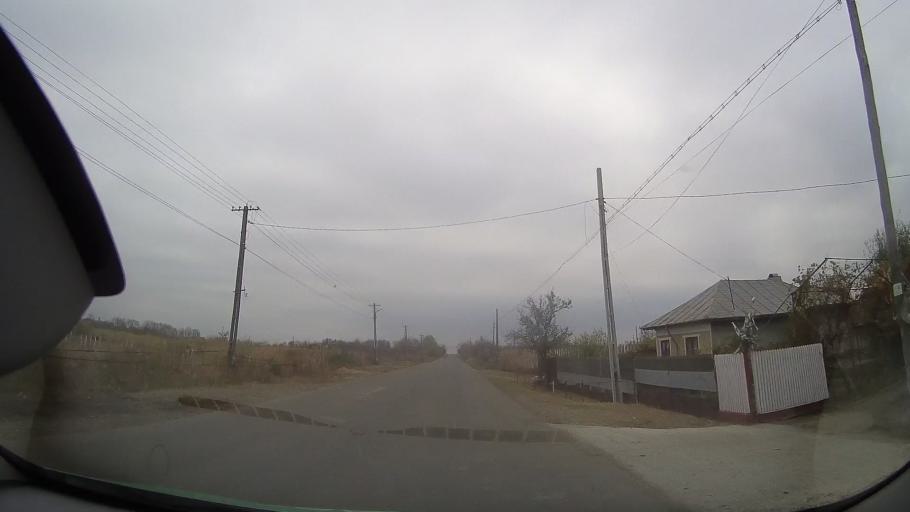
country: RO
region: Buzau
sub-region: Comuna Pogoanele
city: Pogoanele
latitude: 44.9061
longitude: 26.9801
